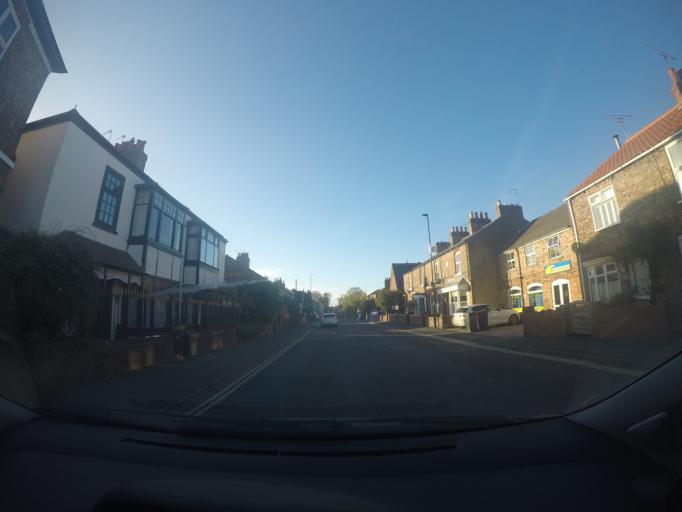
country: GB
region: England
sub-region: City of York
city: Heslington
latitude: 53.9666
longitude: -1.0599
